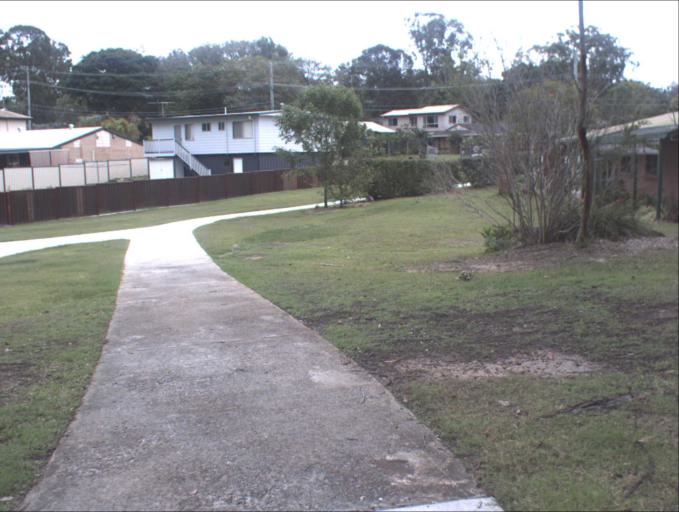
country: AU
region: Queensland
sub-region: Brisbane
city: Sunnybank Hills
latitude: -27.6605
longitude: 153.0528
